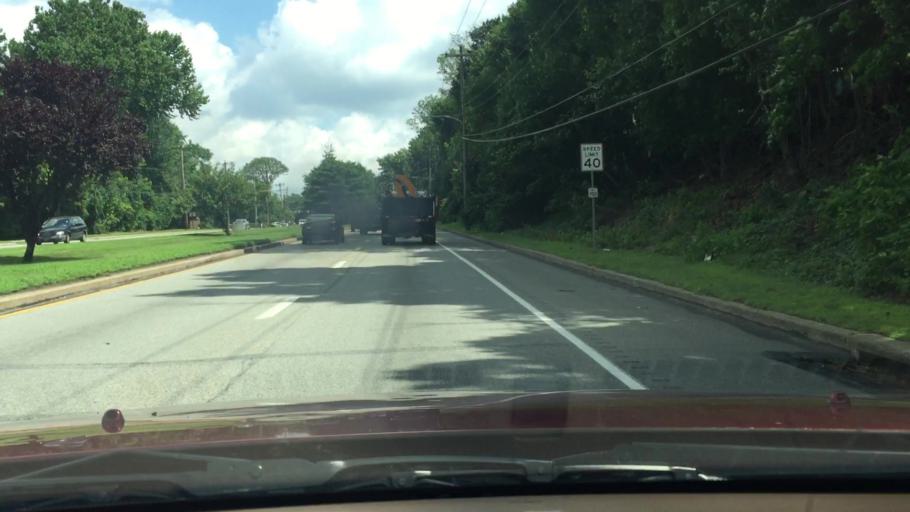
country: US
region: Pennsylvania
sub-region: Delaware County
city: Broomall
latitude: 39.9756
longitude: -75.3307
